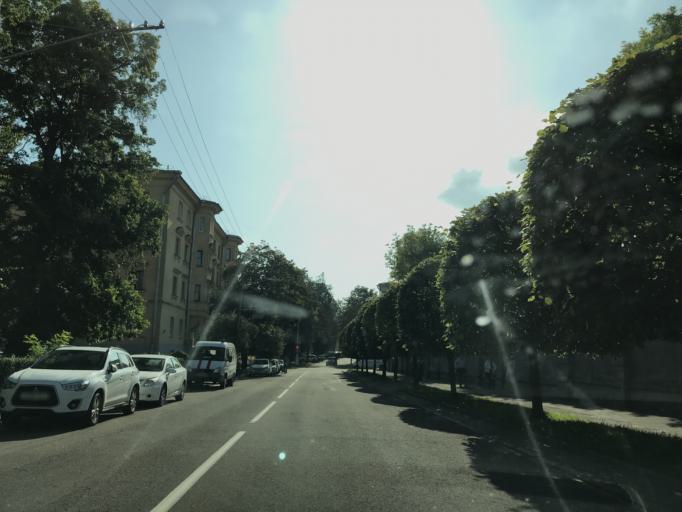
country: BY
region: Minsk
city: Minsk
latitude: 53.9135
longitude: 27.5597
